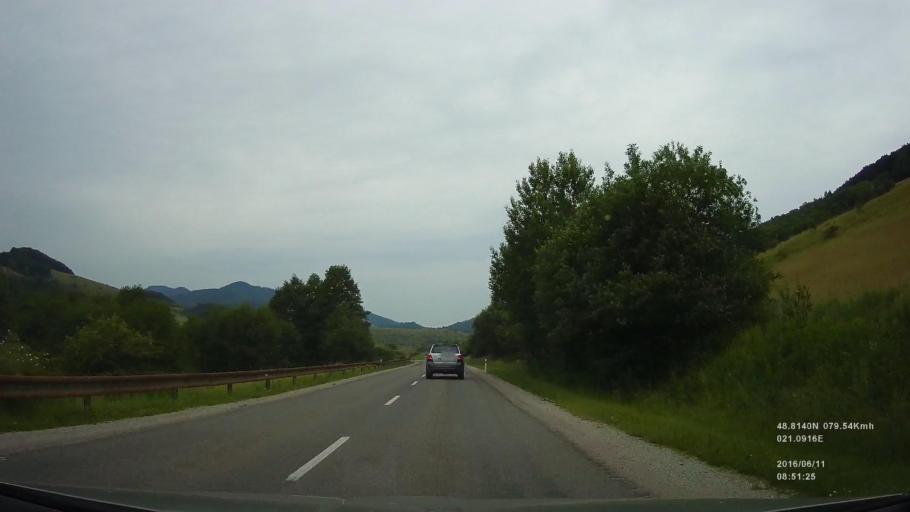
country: SK
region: Kosicky
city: Gelnica
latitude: 48.8082
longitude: 21.0973
